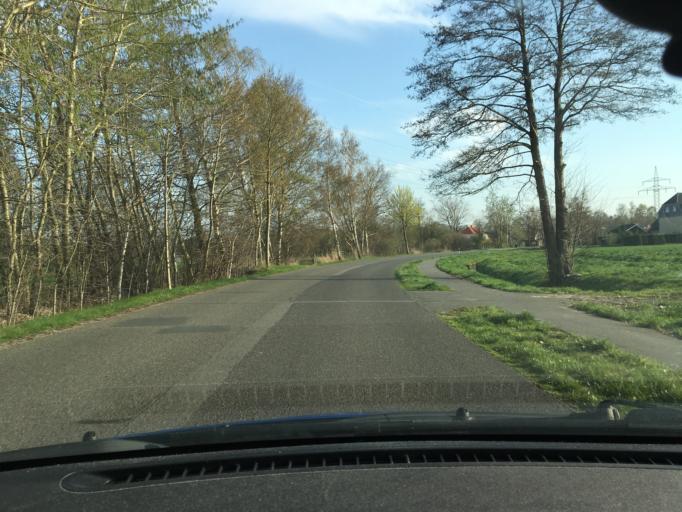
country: DE
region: Lower Saxony
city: Stelle
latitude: 53.4169
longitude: 10.0598
